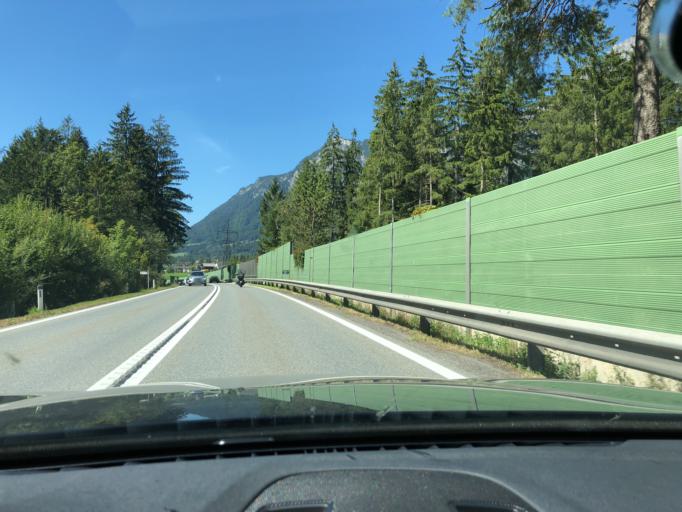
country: AT
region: Vorarlberg
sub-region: Politischer Bezirk Bludenz
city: Innerbraz
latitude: 47.1427
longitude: 9.9196
